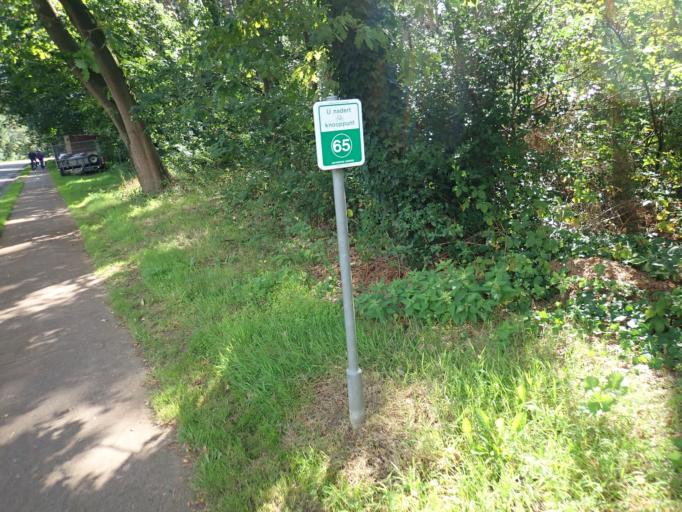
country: BE
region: Flanders
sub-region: Provincie Antwerpen
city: Olen
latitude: 51.1399
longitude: 4.8711
